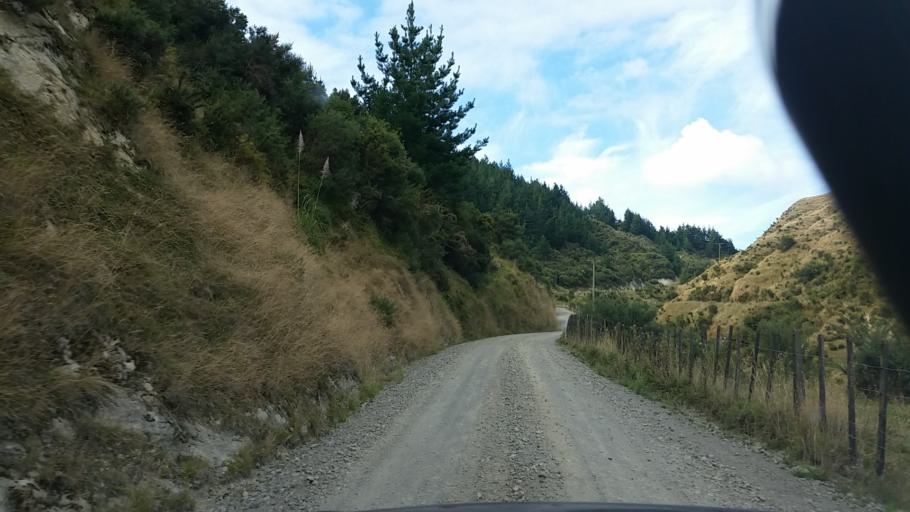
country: NZ
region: Taranaki
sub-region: South Taranaki District
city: Eltham
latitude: -39.2219
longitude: 174.4756
